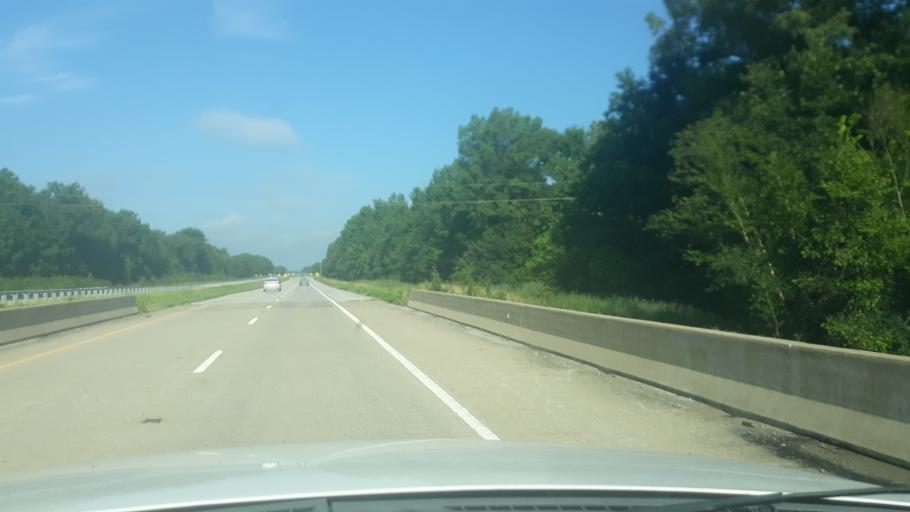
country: US
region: Illinois
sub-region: Saline County
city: Carrier Mills
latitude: 37.7335
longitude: -88.6266
